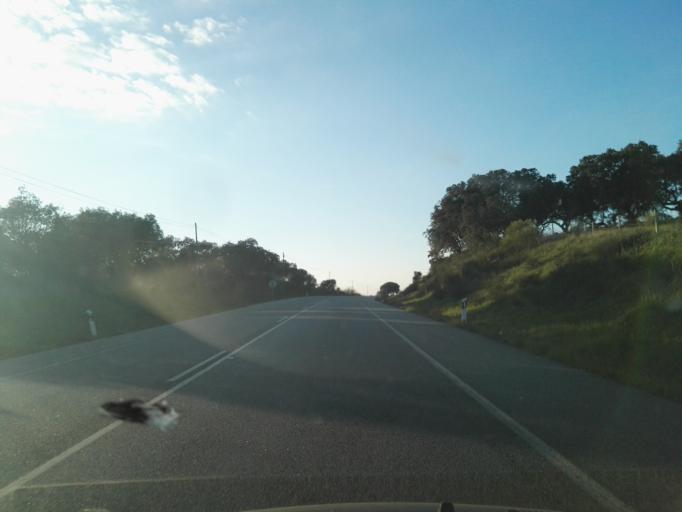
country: PT
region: Evora
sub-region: Montemor-O-Novo
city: Montemor-o-Novo
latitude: 38.6216
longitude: -8.0925
